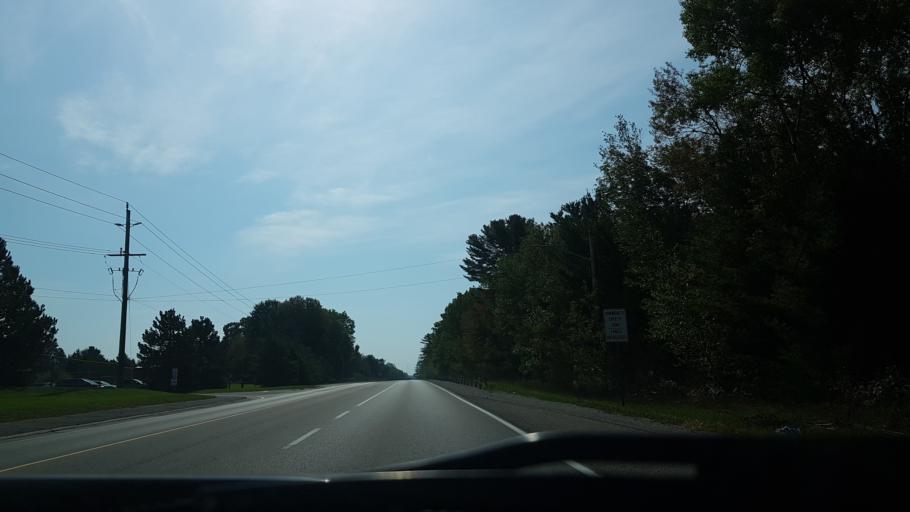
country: CA
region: Ontario
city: Orillia
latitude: 44.7271
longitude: -79.2873
